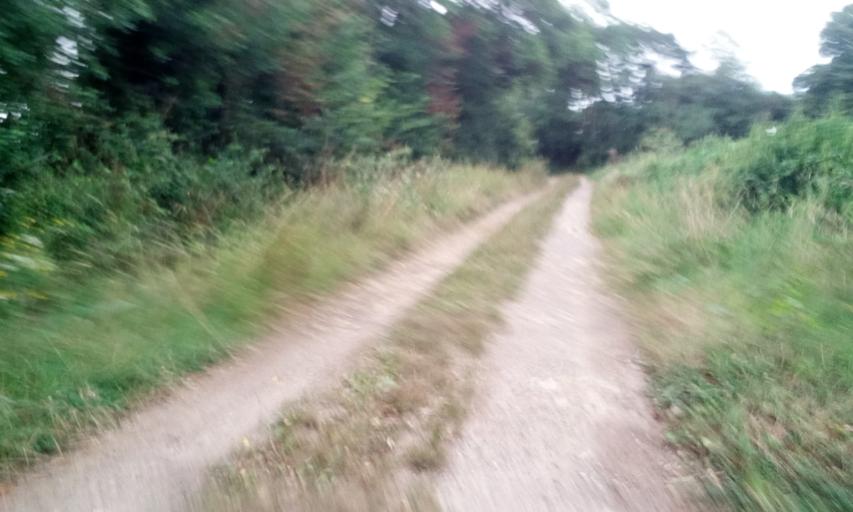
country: FR
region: Lower Normandy
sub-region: Departement du Calvados
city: Sannerville
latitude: 49.1879
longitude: -0.2168
